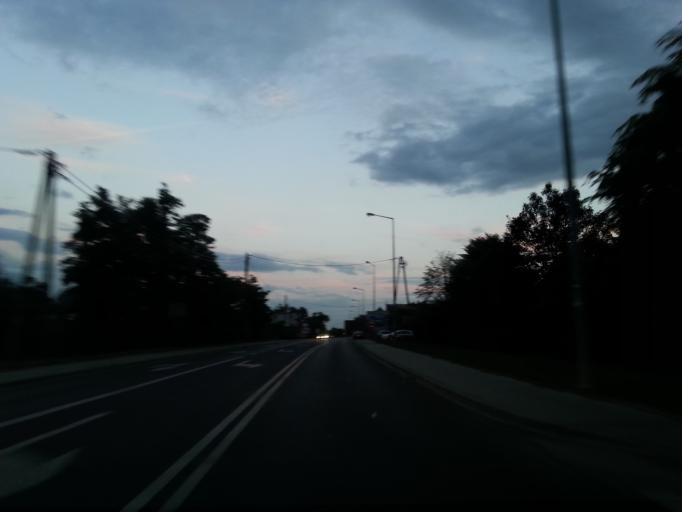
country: PL
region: Lower Silesian Voivodeship
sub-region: Powiat wroclawski
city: Bielany Wroclawskie
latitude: 51.0320
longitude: 16.9679
